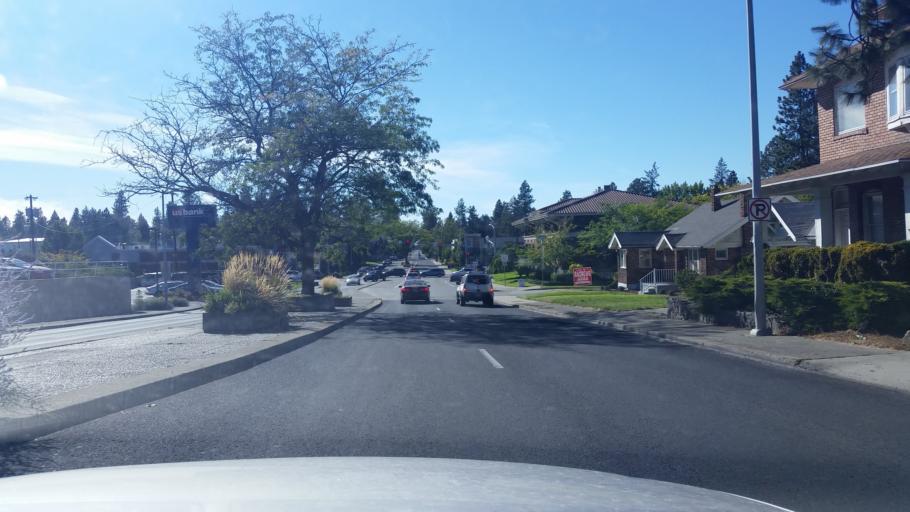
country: US
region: Washington
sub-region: Spokane County
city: Spokane
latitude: 47.6282
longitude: -117.3999
